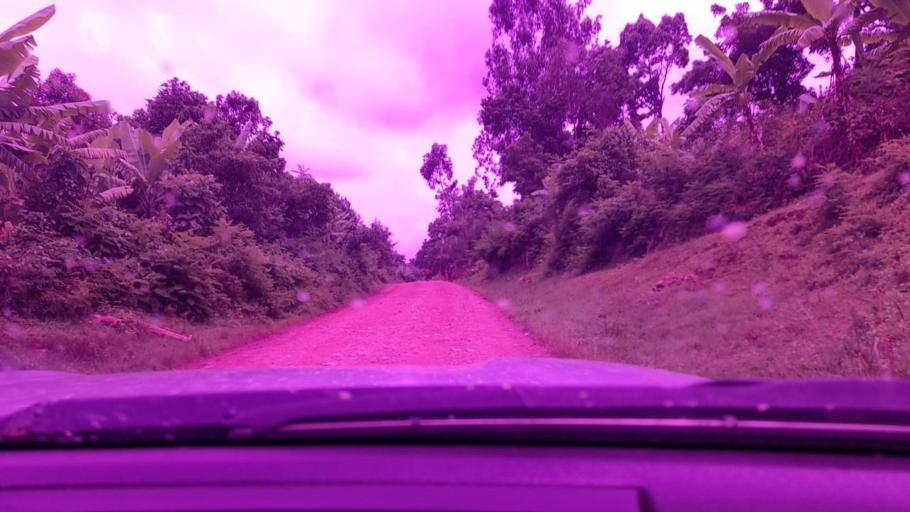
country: ET
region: Southern Nations, Nationalities, and People's Region
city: Bonga
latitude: 7.5449
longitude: 35.8778
